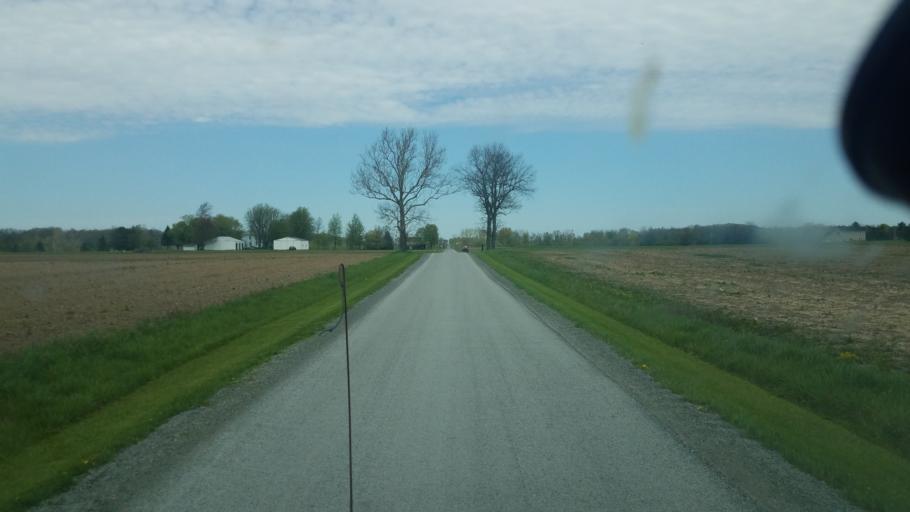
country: US
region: Ohio
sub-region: Hardin County
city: Ada
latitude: 40.7873
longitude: -83.8615
